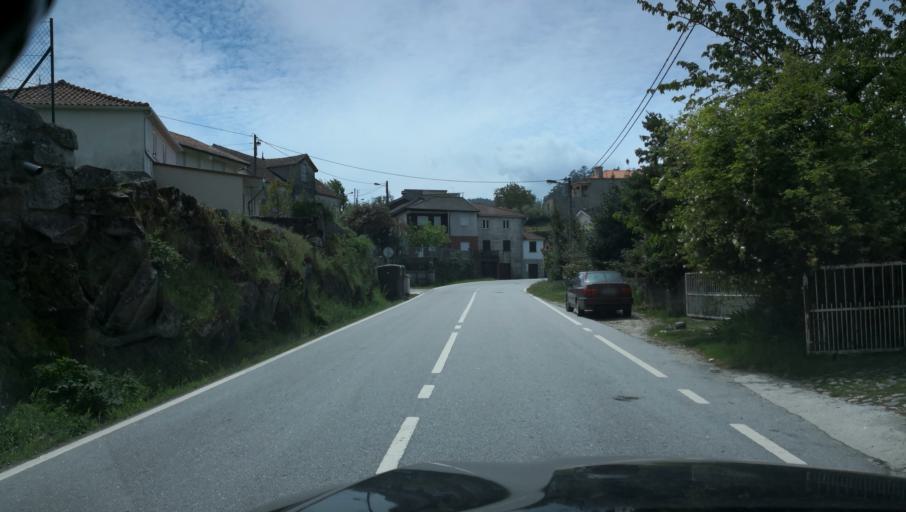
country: PT
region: Vila Real
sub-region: Vila Real
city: Vila Real
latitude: 41.2824
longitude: -7.8127
